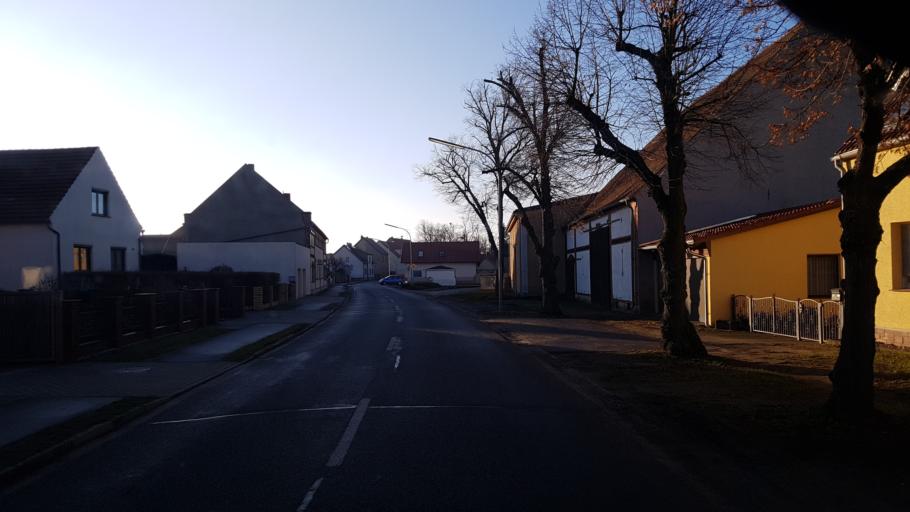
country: DE
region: Saxony
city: Arzberg
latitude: 51.5205
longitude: 13.1833
